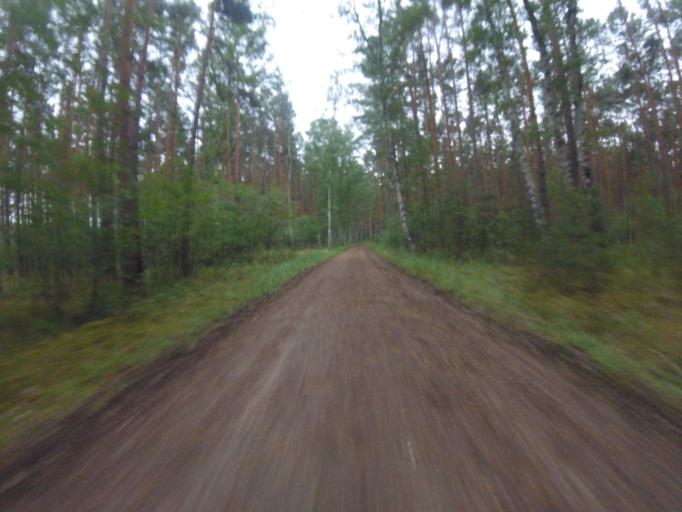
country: DE
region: Brandenburg
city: Gross Koris
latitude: 52.2063
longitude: 13.6987
